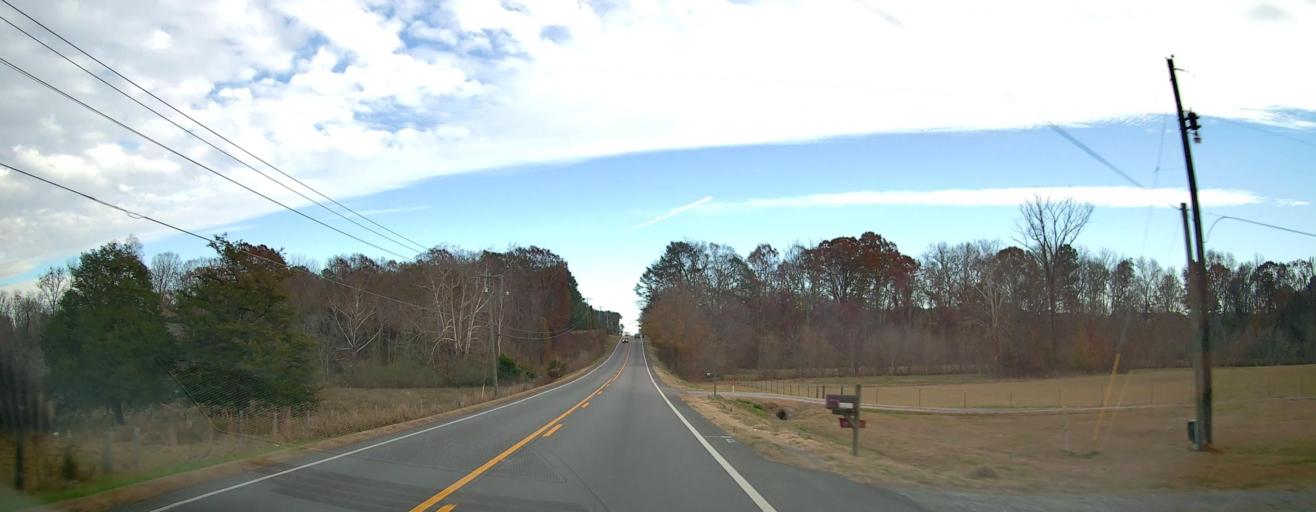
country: US
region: Alabama
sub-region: Morgan County
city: Priceville
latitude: 34.4536
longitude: -86.7682
